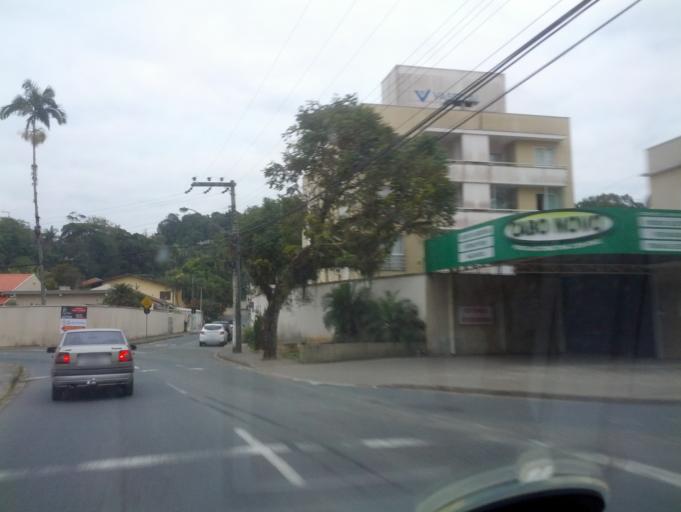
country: BR
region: Santa Catarina
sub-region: Blumenau
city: Blumenau
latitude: -26.8760
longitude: -49.0810
